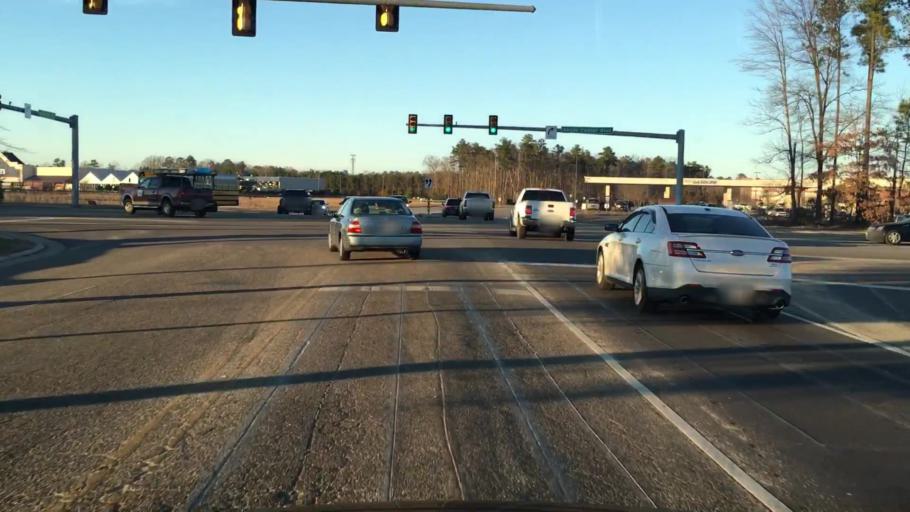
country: US
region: Virginia
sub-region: Chesterfield County
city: Bon Air
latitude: 37.5116
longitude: -77.6069
